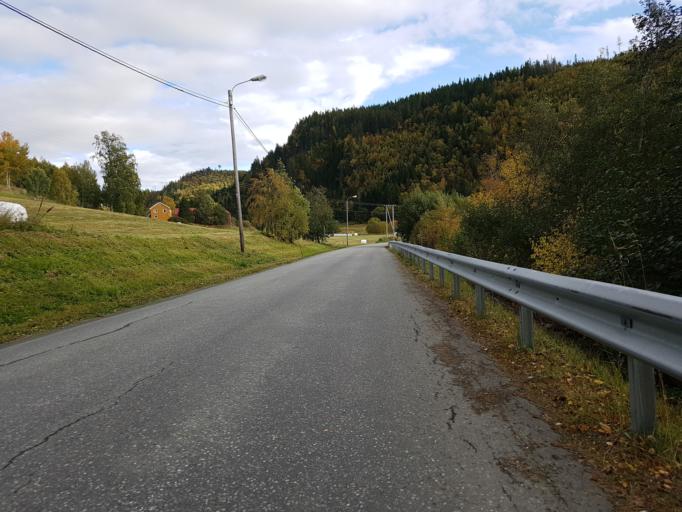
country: NO
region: Sor-Trondelag
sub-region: Klaebu
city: Klaebu
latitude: 63.3979
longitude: 10.5521
